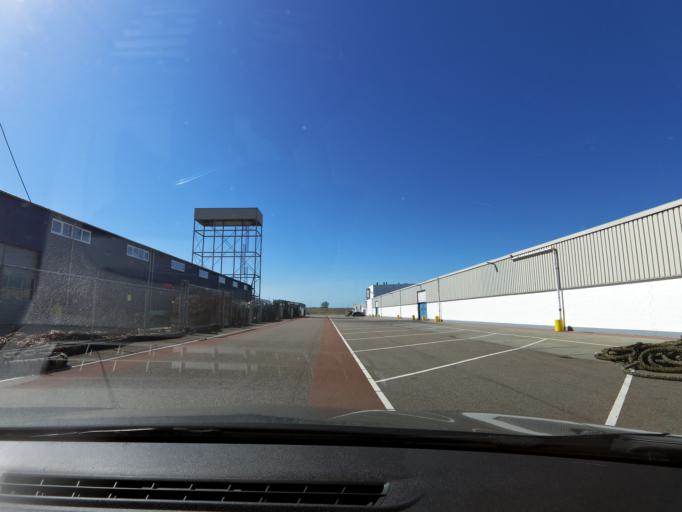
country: NL
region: South Holland
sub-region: Gemeente Goeree-Overflakkee
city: Goedereede
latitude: 51.8249
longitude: 4.0324
